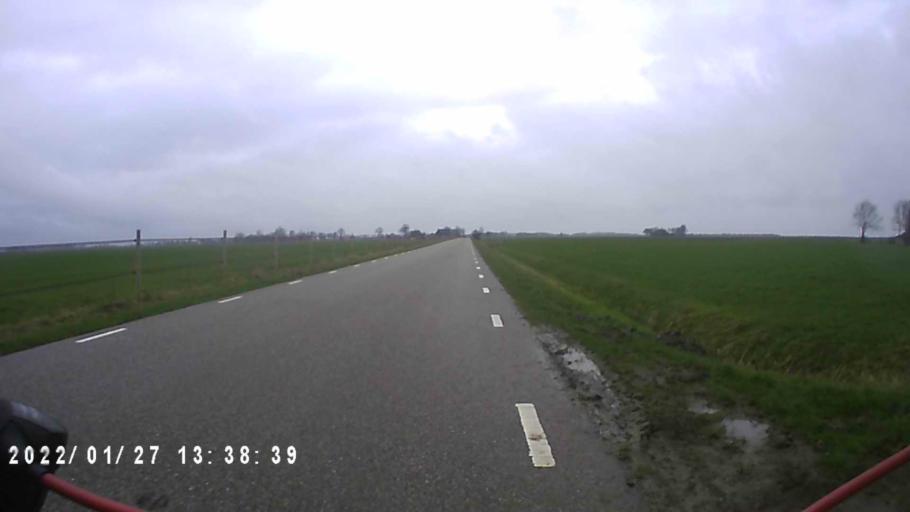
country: NL
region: Friesland
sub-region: Gemeente Kollumerland en Nieuwkruisland
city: Kollum
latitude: 53.2970
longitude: 6.2223
